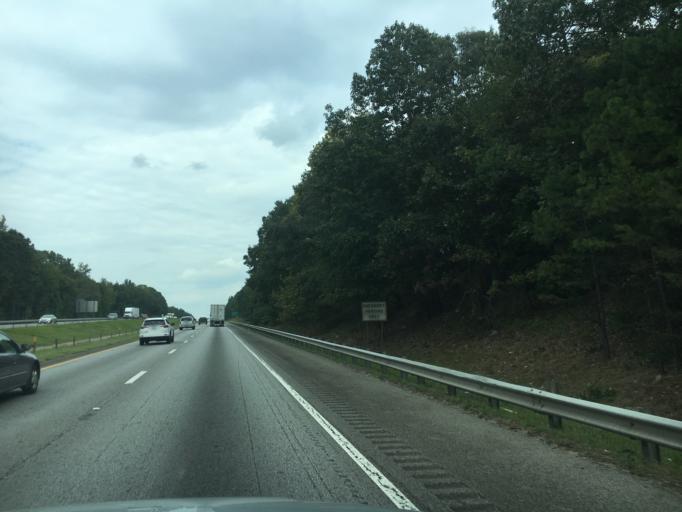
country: US
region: South Carolina
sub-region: Anderson County
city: Centerville
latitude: 34.5385
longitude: -82.8212
